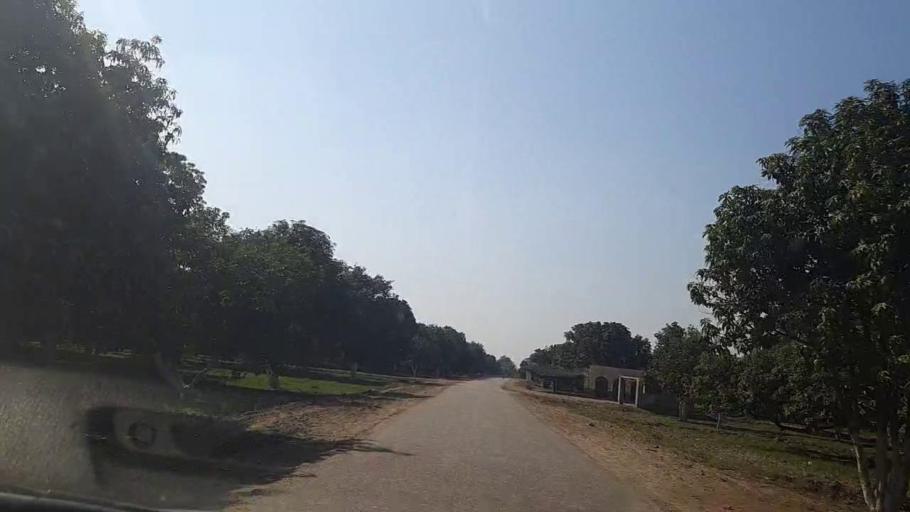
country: PK
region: Sindh
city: Sakrand
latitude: 26.0204
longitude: 68.3523
